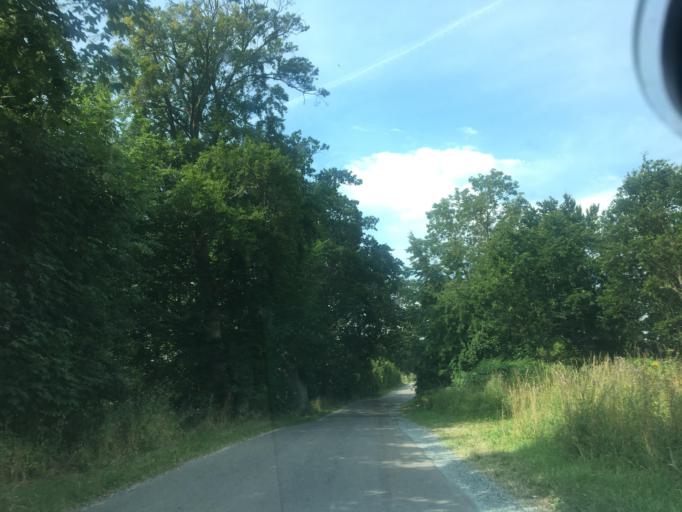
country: DK
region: Zealand
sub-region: Faxe Kommune
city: Fakse
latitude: 55.1845
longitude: 12.1003
